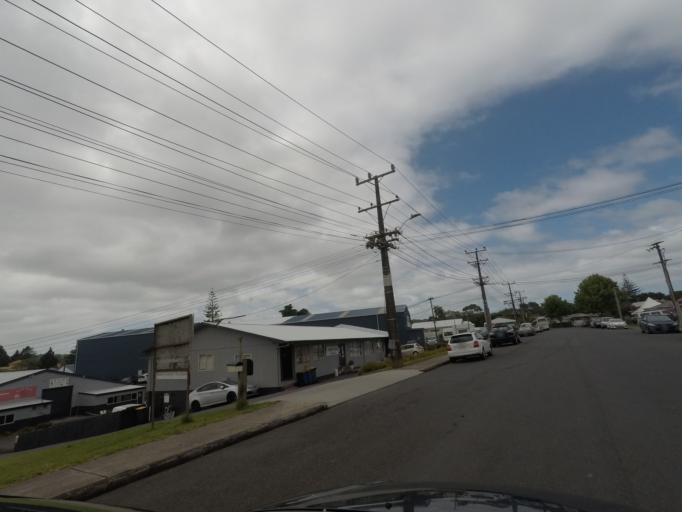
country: NZ
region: Auckland
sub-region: Auckland
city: Waitakere
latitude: -36.9074
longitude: 174.6374
